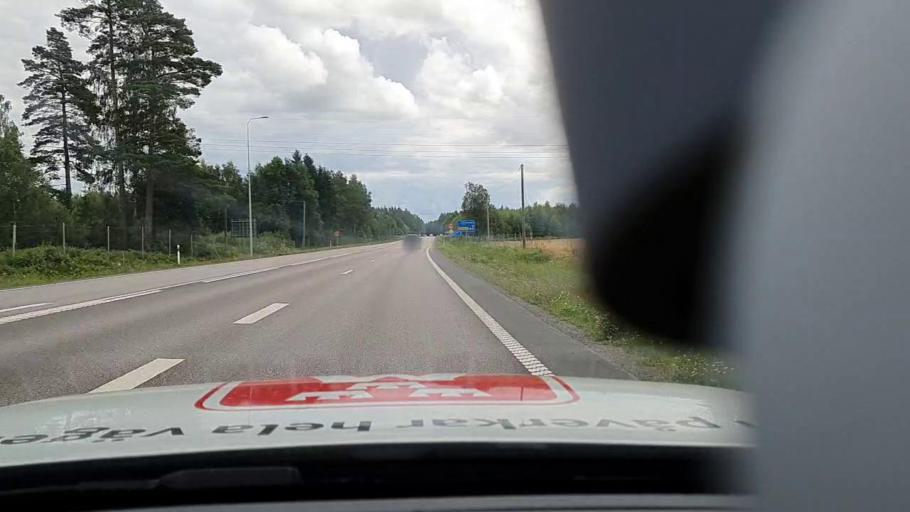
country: SE
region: Vaestra Goetaland
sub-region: Lidkopings Kommun
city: Lidkoping
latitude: 58.4783
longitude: 13.2030
